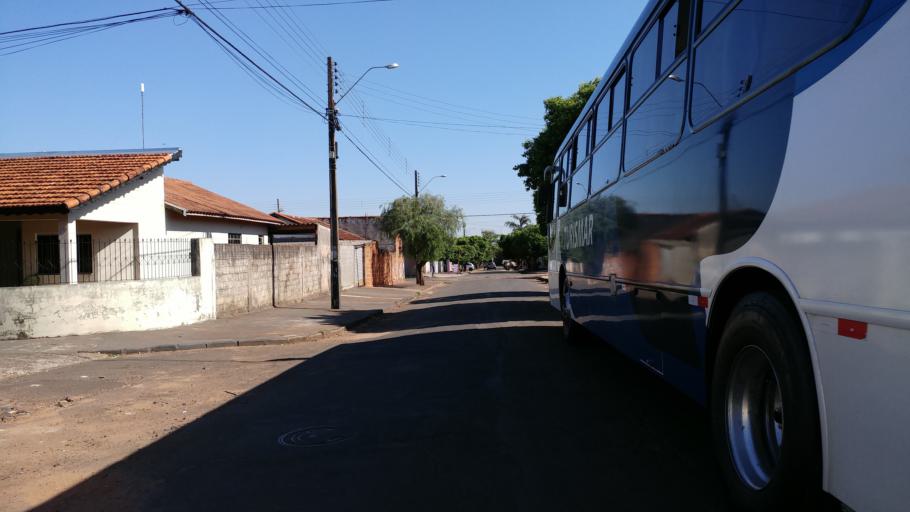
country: BR
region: Sao Paulo
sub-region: Paraguacu Paulista
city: Paraguacu Paulista
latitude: -22.4337
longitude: -50.5822
